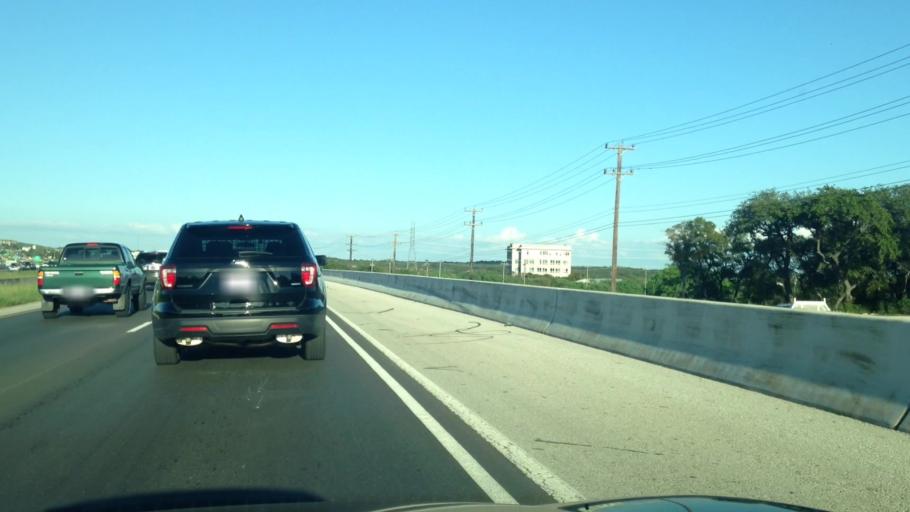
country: US
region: Texas
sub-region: Bexar County
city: Shavano Park
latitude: 29.5929
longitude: -98.5798
